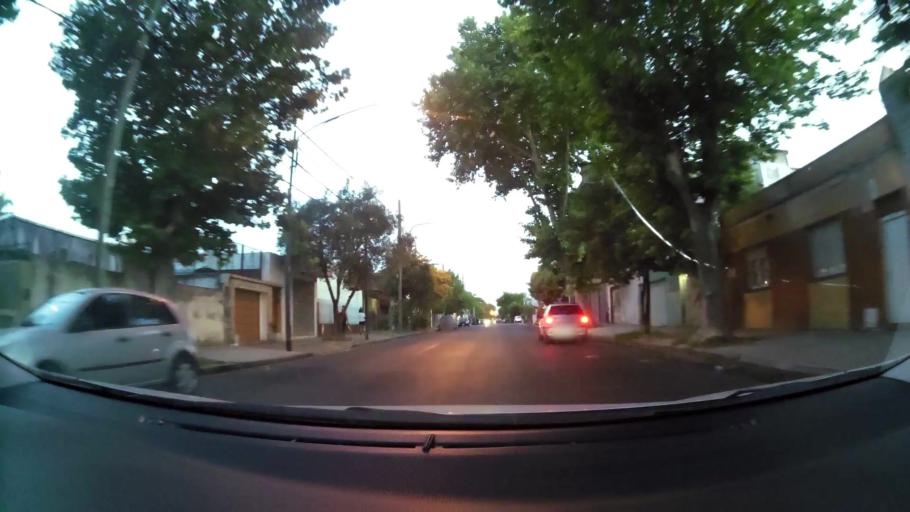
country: AR
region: Buenos Aires F.D.
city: Villa Lugano
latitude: -34.6892
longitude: -58.4699
